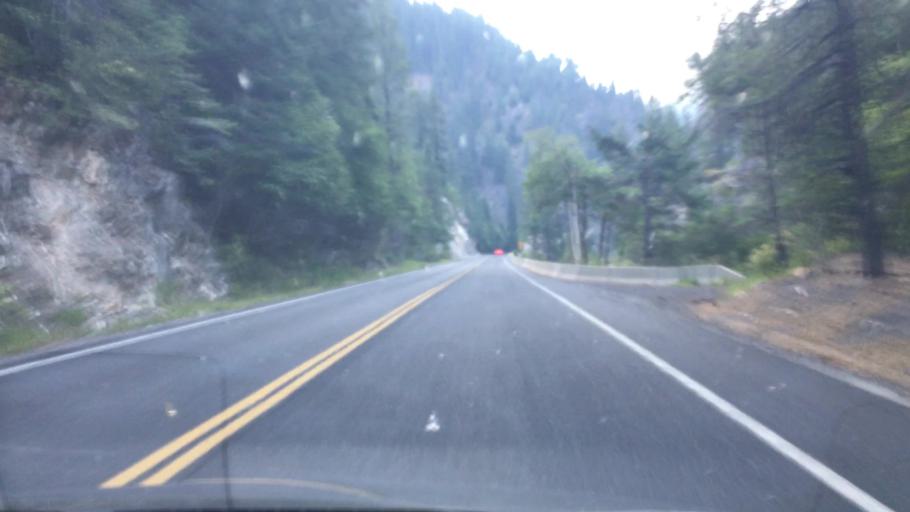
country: US
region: Idaho
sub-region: Valley County
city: McCall
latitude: 45.1398
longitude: -116.2870
